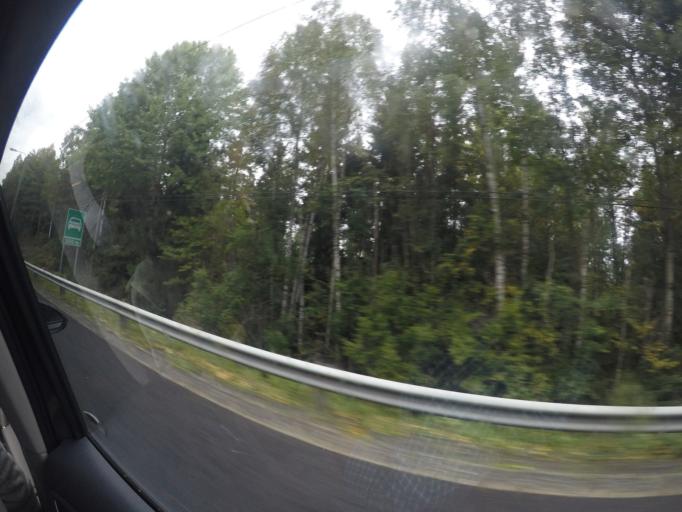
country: FI
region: Pirkanmaa
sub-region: Tampere
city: Kangasala
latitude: 61.4455
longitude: 24.1111
